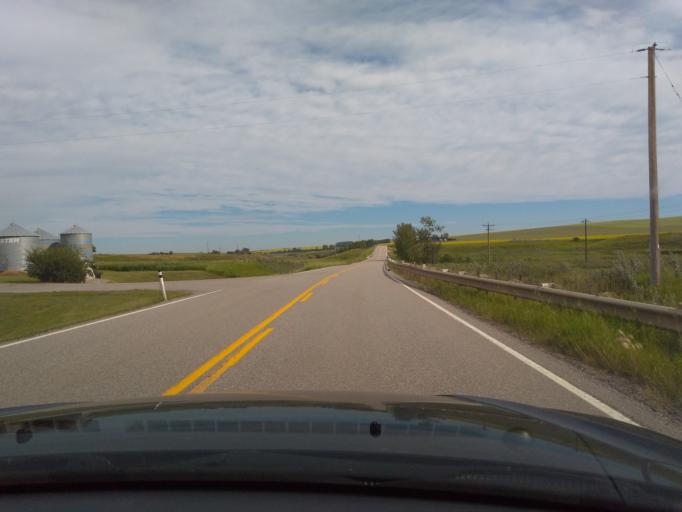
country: CA
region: Alberta
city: Carstairs
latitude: 51.5147
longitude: -114.3068
